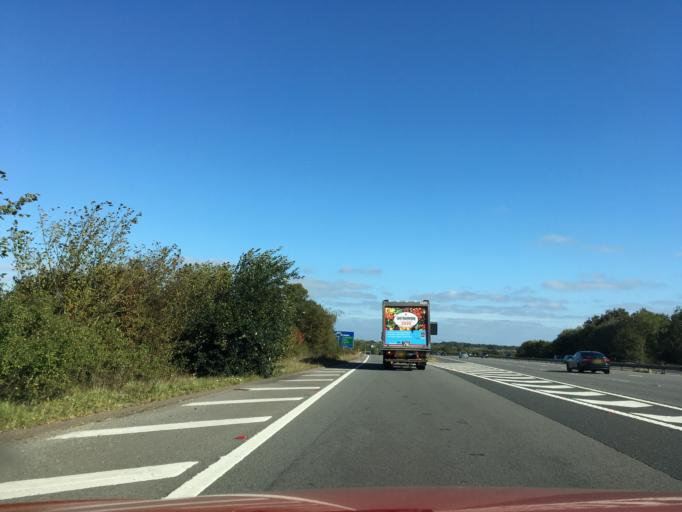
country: GB
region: England
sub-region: West Berkshire
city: Winterbourne
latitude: 51.4530
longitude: -1.3195
